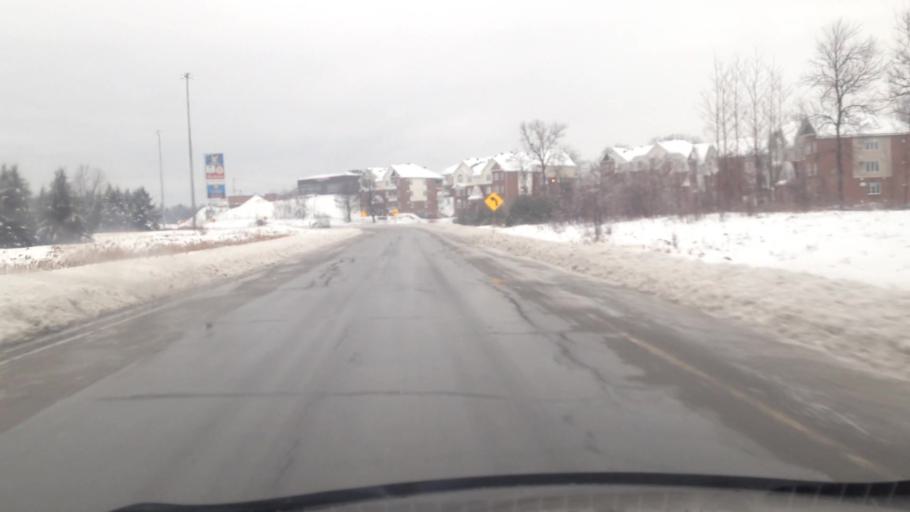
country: CA
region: Quebec
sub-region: Laurentides
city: Saint-Jerome
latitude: 45.7758
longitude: -74.0194
